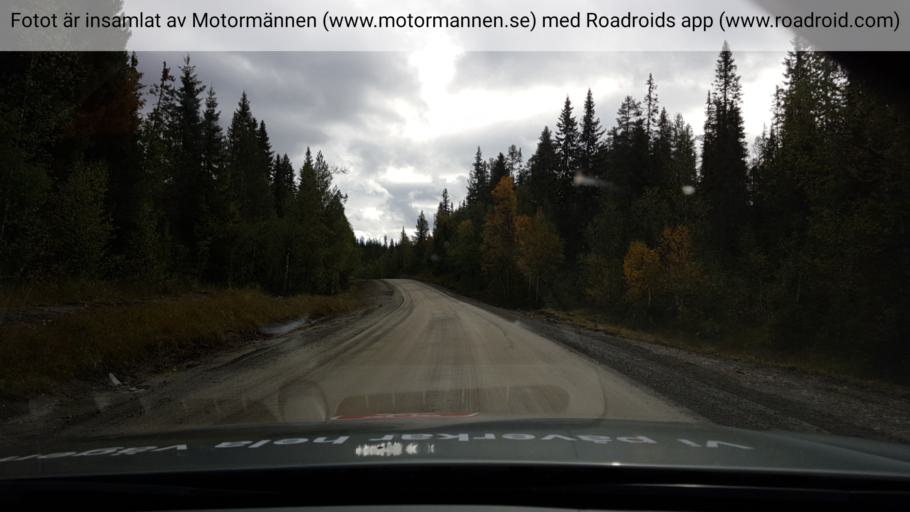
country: SE
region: Jaemtland
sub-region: Are Kommun
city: Are
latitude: 63.7195
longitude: 12.6083
